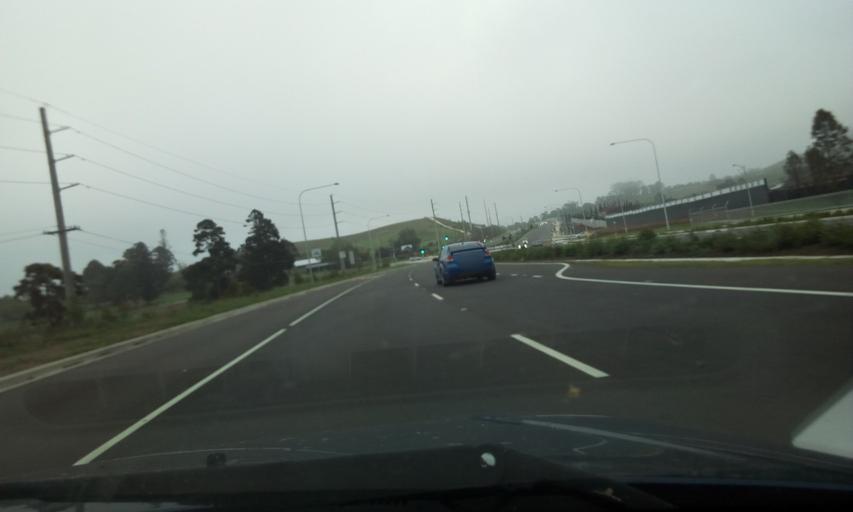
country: AU
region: New South Wales
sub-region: Camden
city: Narellan
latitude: -34.0281
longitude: 150.7271
